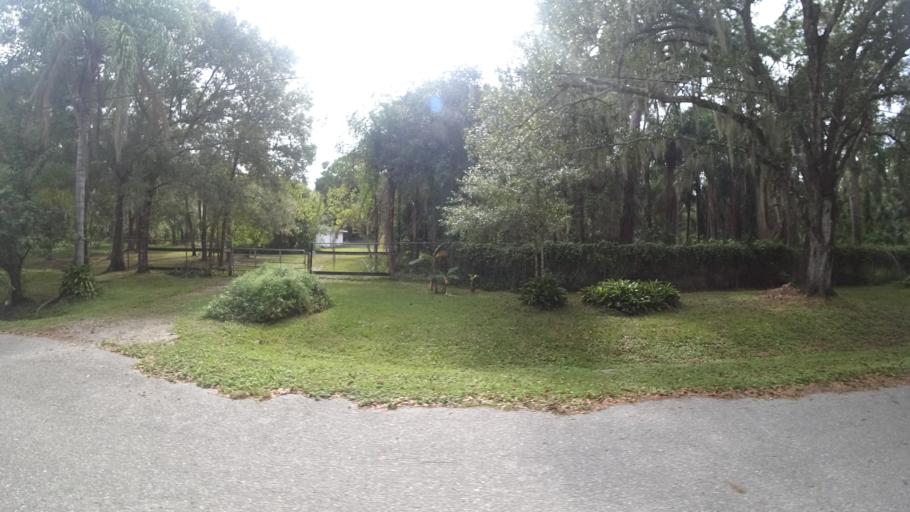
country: US
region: Florida
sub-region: Sarasota County
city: North Sarasota
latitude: 27.3870
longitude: -82.5269
